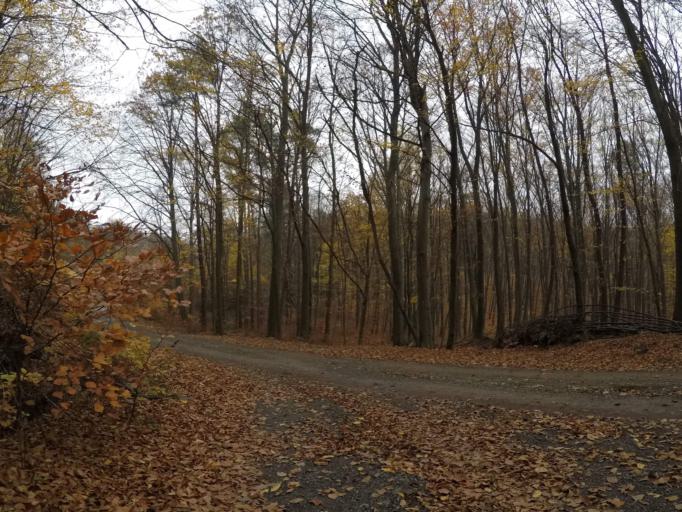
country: SK
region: Presovsky
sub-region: Okres Presov
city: Presov
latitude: 48.8850
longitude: 21.1970
